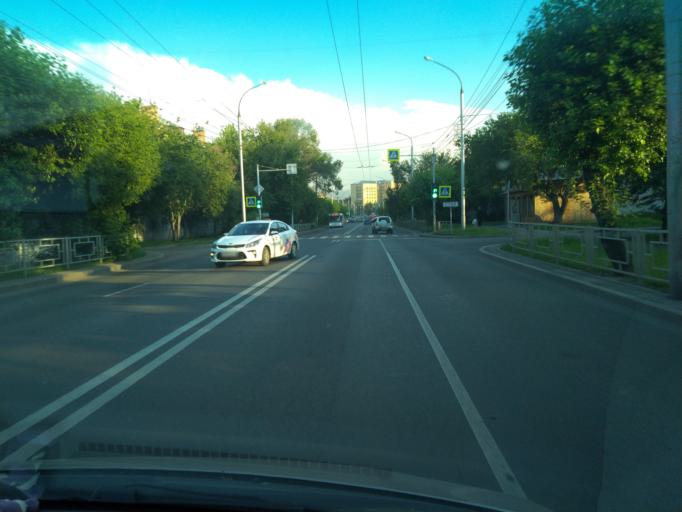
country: RU
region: Krasnoyarskiy
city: Krasnoyarsk
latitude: 56.0299
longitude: 92.9074
